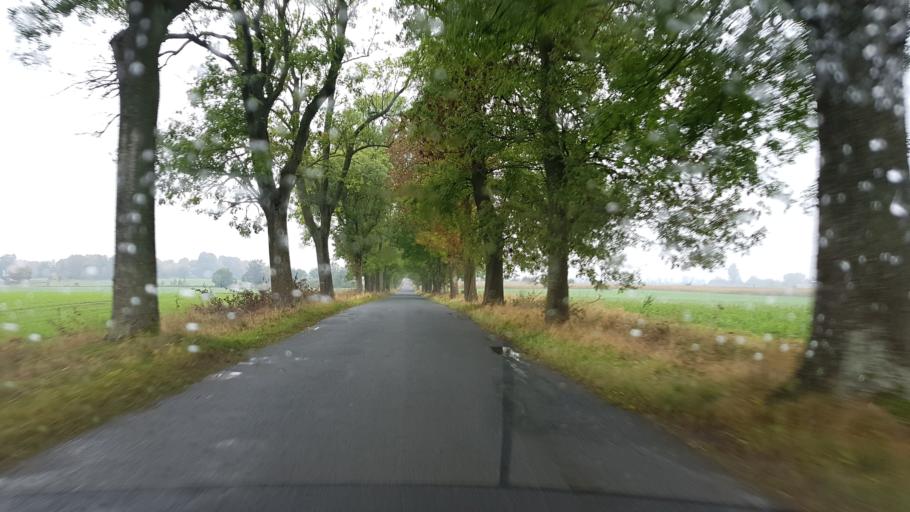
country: PL
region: Greater Poland Voivodeship
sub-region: Powiat zlotowski
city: Tarnowka
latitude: 53.3432
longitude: 16.8745
